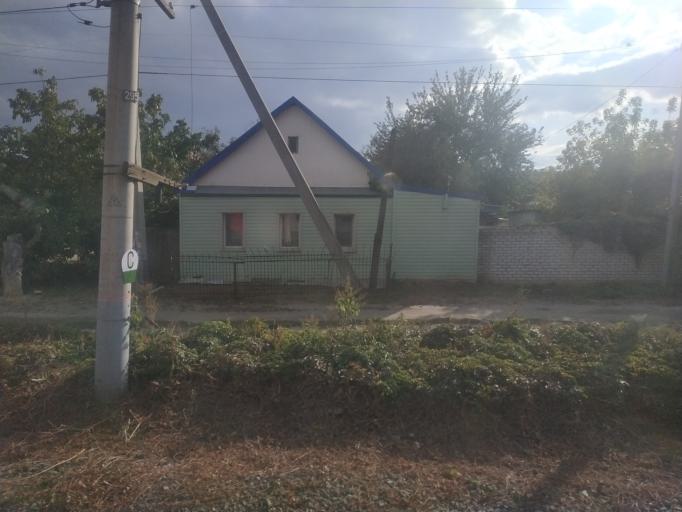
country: RU
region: Volgograd
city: Krasnoslobodsk
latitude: 48.5092
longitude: 44.5349
